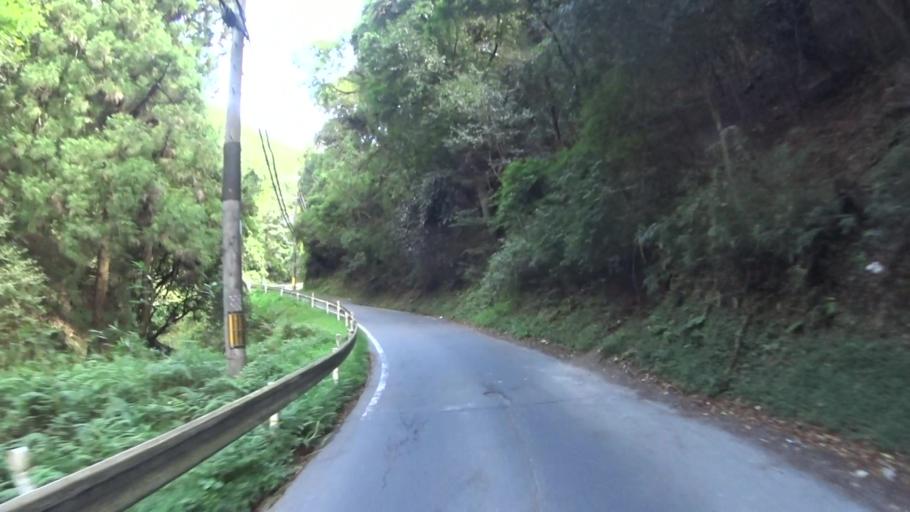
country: JP
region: Kyoto
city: Uji
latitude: 34.9239
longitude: 135.8197
